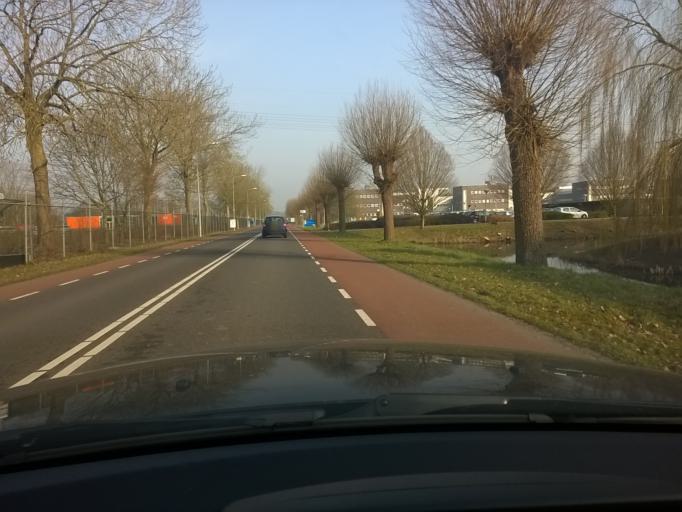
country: NL
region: Groningen
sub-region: Gemeente Groningen
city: Korrewegwijk
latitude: 53.2401
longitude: 6.5299
